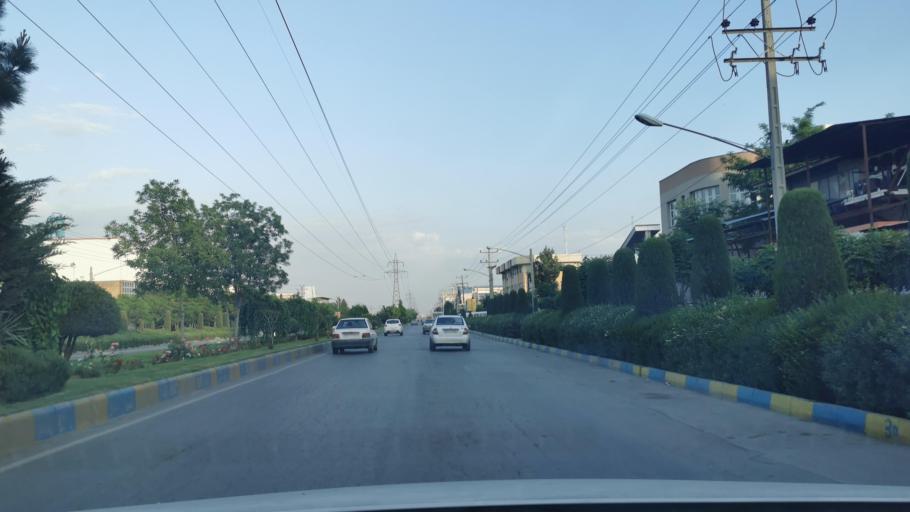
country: IR
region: Razavi Khorasan
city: Torqabeh
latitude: 36.4263
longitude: 59.4224
